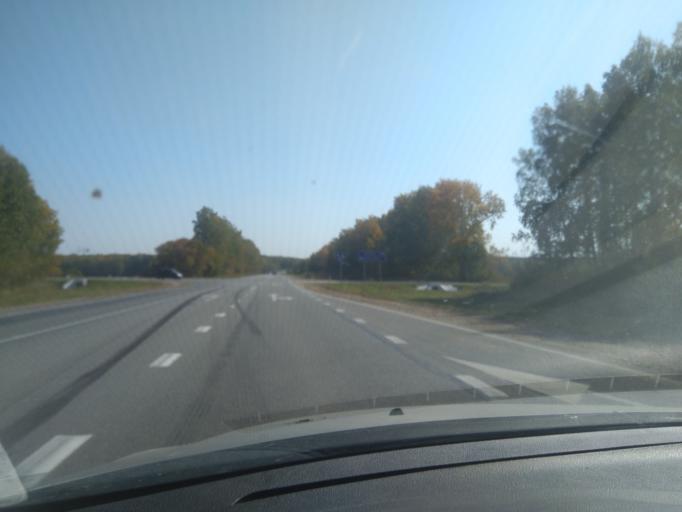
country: RU
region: Sverdlovsk
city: Sovkhoznyy
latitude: 56.5434
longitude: 61.3891
